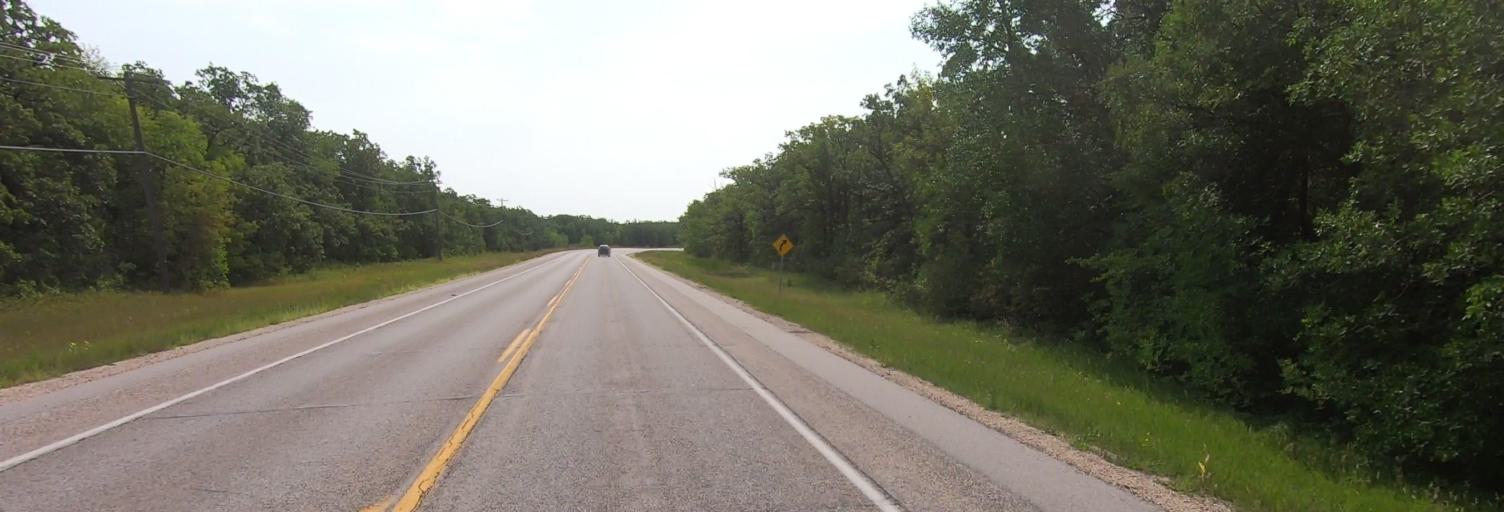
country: CA
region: Manitoba
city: Niverville
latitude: 49.7287
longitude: -97.0946
